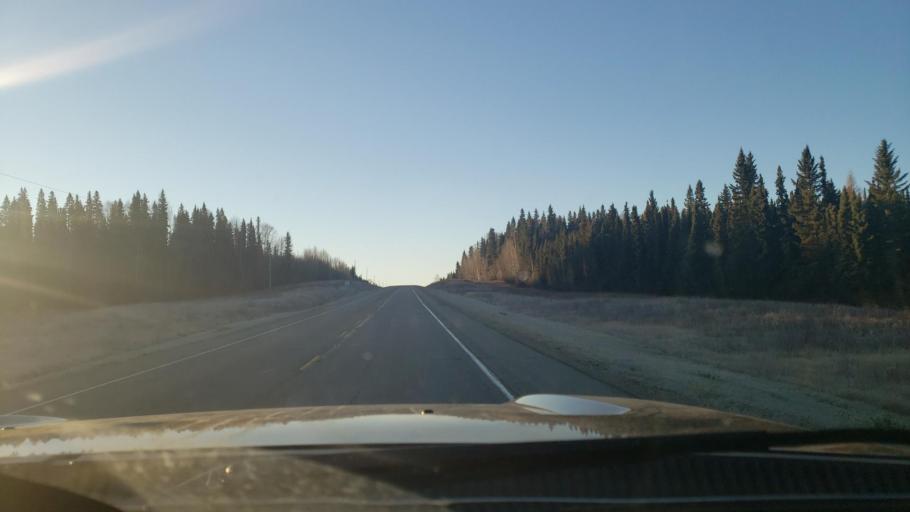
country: CA
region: British Columbia
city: Fort Nelson
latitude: 58.4314
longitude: -122.7136
